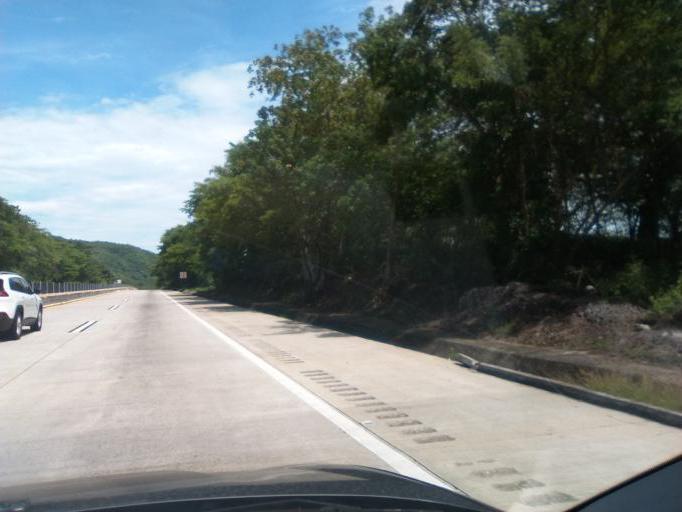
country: MX
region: Guerrero
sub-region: Acapulco de Juarez
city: Pueblo Madero (El Playon)
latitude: 17.0665
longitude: -99.6286
